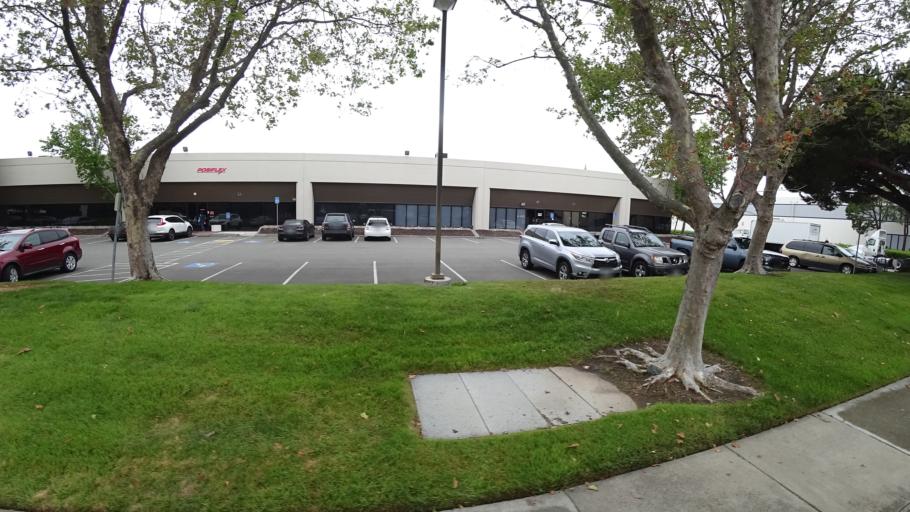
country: US
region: California
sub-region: Alameda County
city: Union City
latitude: 37.6180
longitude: -122.0549
